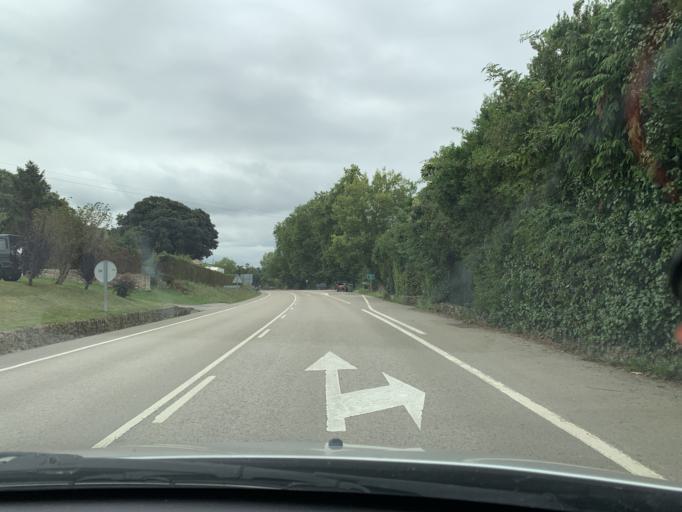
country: ES
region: Cantabria
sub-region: Provincia de Cantabria
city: Santillana
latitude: 43.3846
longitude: -4.1076
